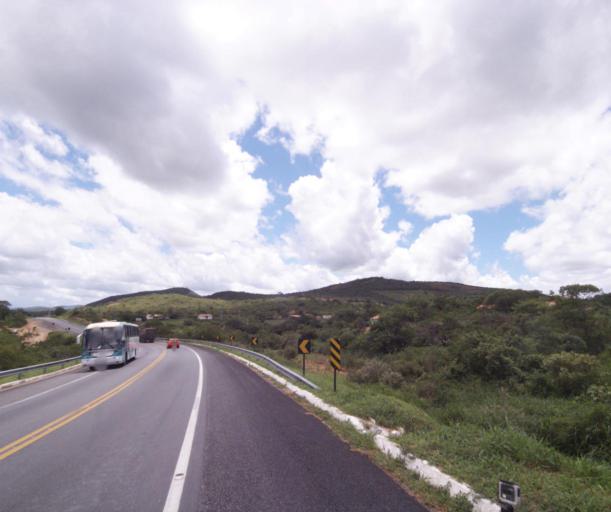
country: BR
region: Bahia
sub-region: Pocoes
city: Pocoes
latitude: -14.3619
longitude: -40.3405
